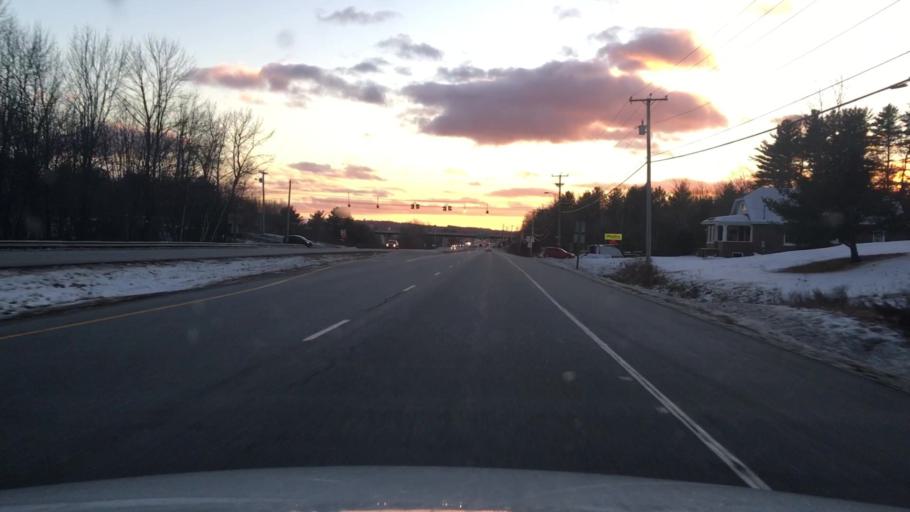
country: US
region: Maine
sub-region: Androscoggin County
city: Auburn
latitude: 44.0440
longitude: -70.2593
